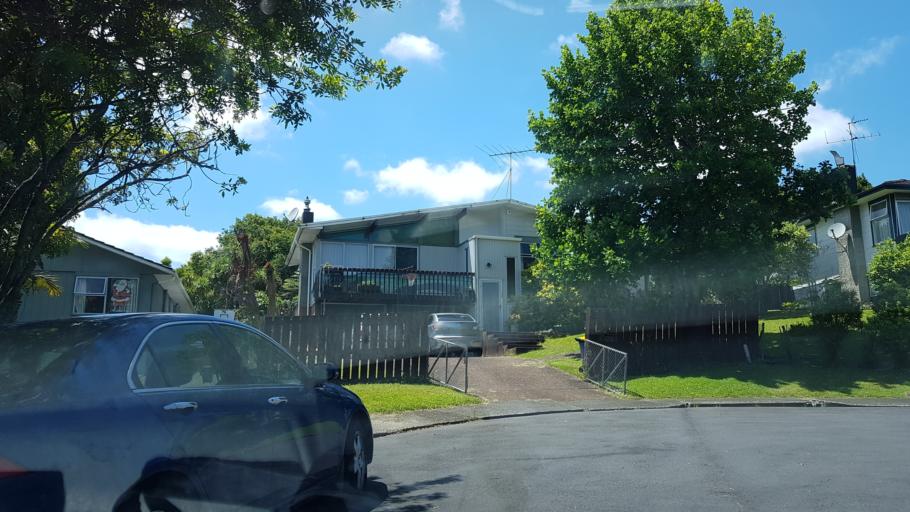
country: NZ
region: Auckland
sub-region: Auckland
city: North Shore
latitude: -36.7846
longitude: 174.7205
